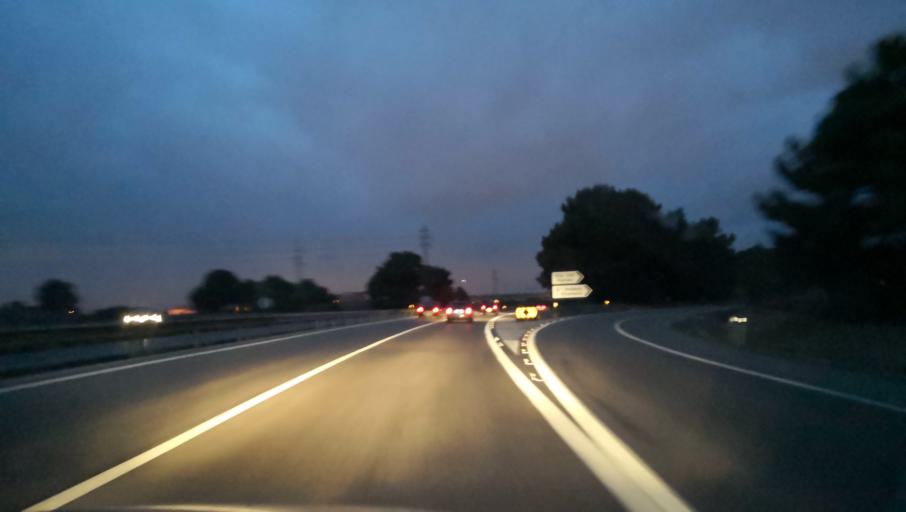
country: PT
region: Setubal
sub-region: Barreiro
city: Santo Antonio da Charneca
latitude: 38.6208
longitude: -9.0345
